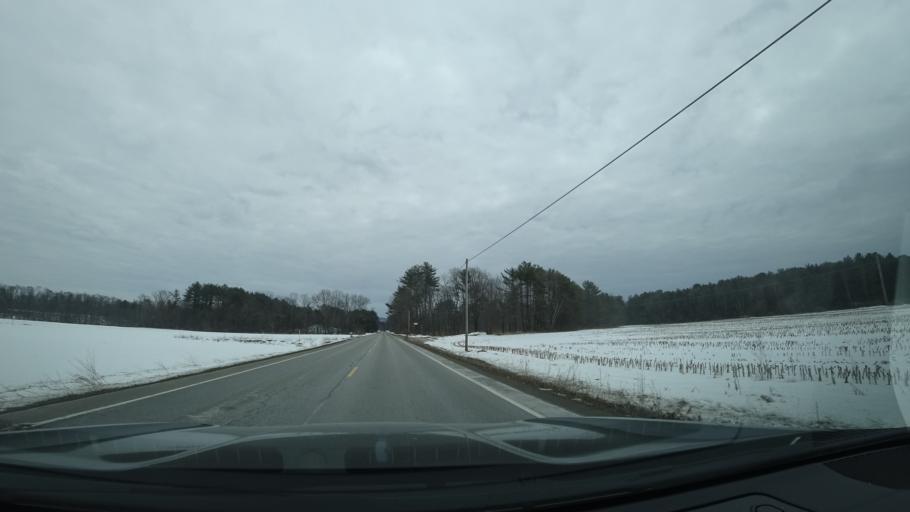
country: US
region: New York
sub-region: Washington County
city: Cambridge
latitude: 43.1501
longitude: -73.3767
